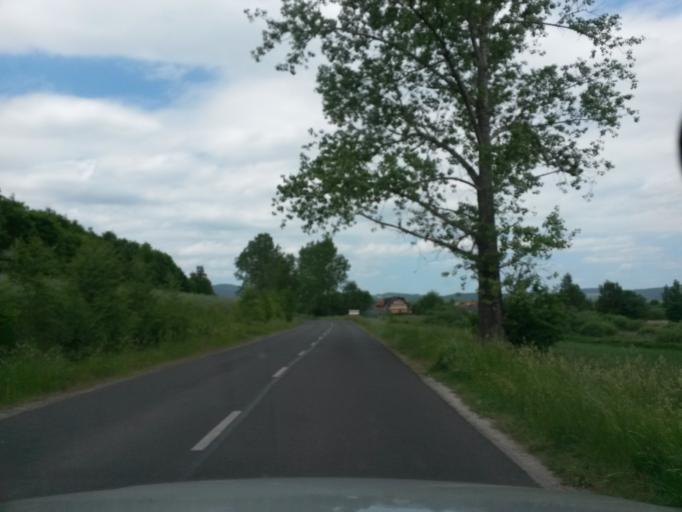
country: PL
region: Lower Silesian Voivodeship
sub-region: Powiat jeleniogorski
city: Podgorzyn
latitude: 50.8390
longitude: 15.6578
